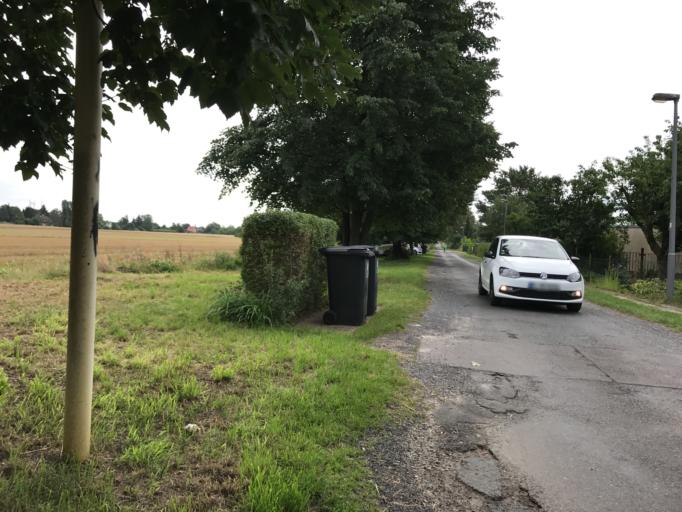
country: DE
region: Berlin
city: Karow
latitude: 52.6082
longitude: 13.4856
